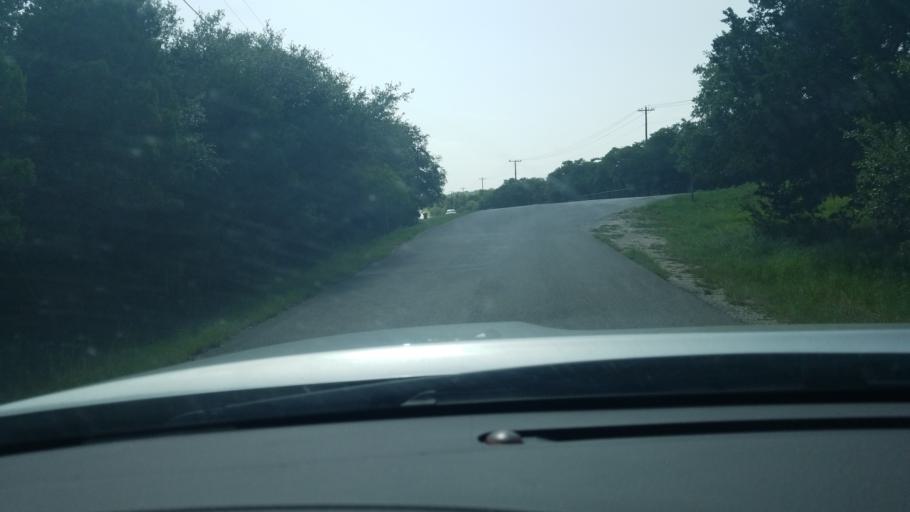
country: US
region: Texas
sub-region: Comal County
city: Bulverde
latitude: 29.7970
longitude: -98.4443
